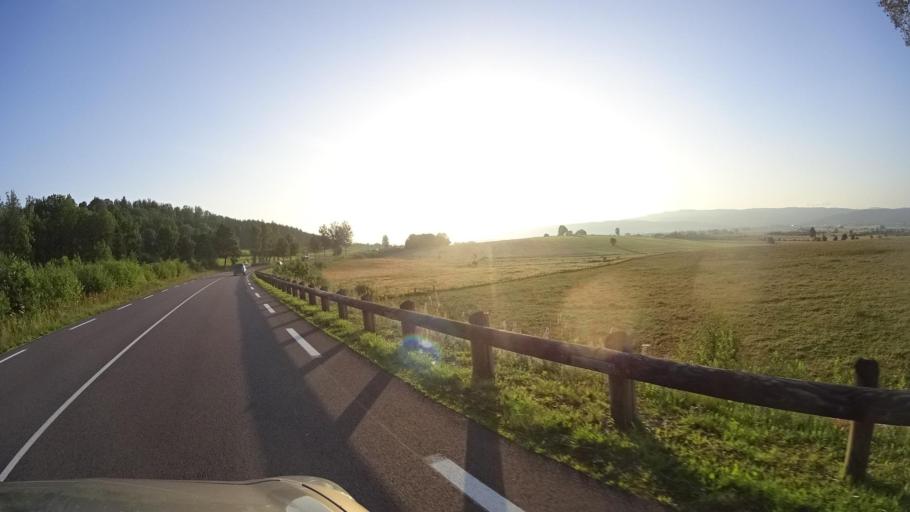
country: FR
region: Franche-Comte
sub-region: Departement du Doubs
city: Doubs
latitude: 46.9145
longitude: 6.2845
